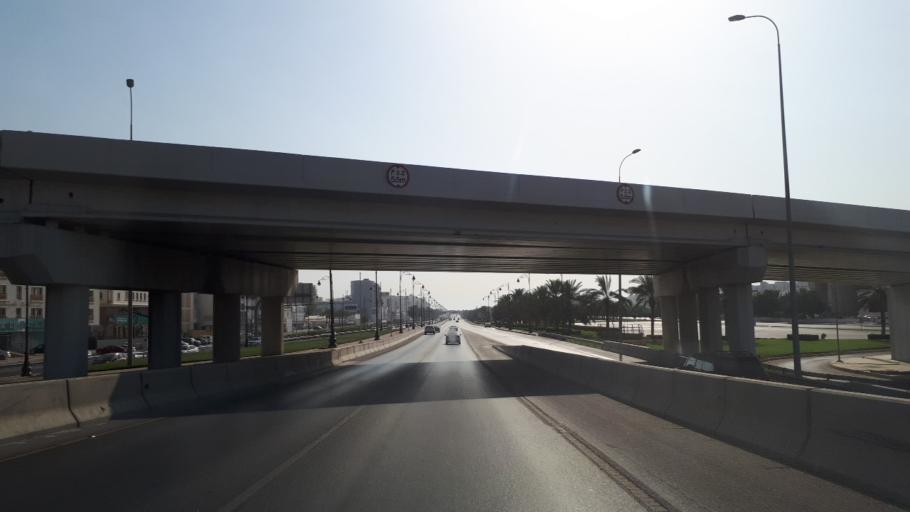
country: OM
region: Muhafazat Masqat
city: Bawshar
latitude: 23.5972
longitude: 58.4403
